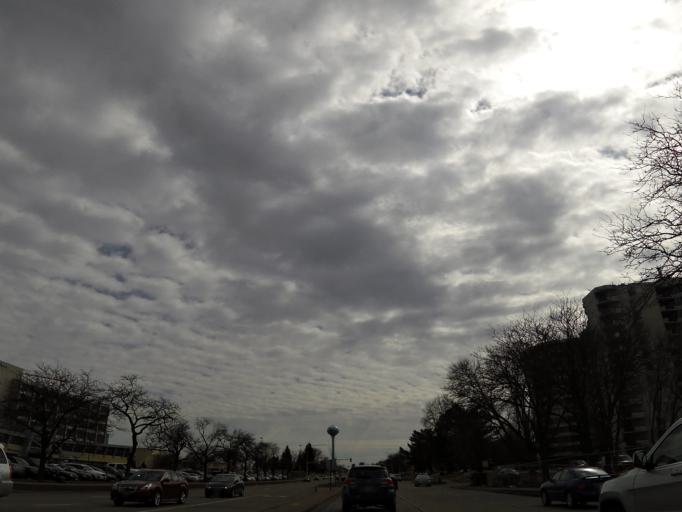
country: US
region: Minnesota
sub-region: Hennepin County
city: Edina
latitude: 44.8856
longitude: -93.3290
